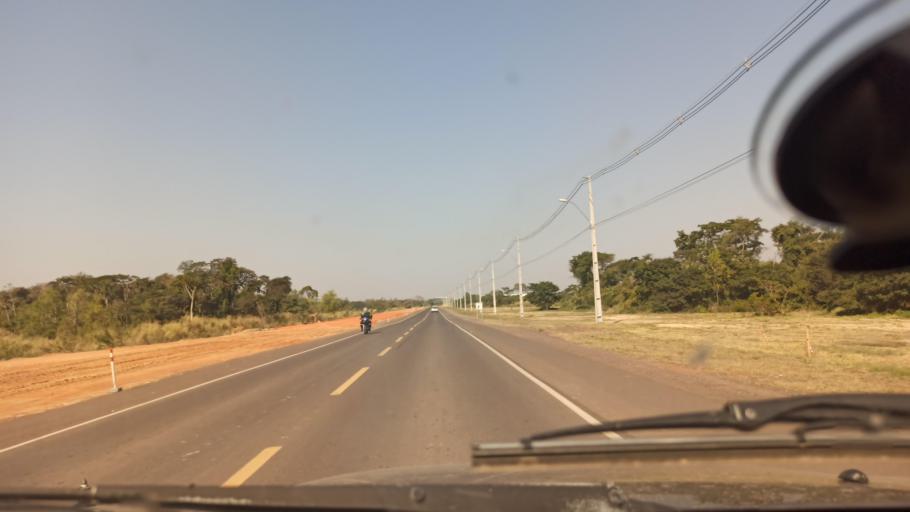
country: PY
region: Central
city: Colonia Mariano Roque Alonso
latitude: -25.1899
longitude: -57.5806
